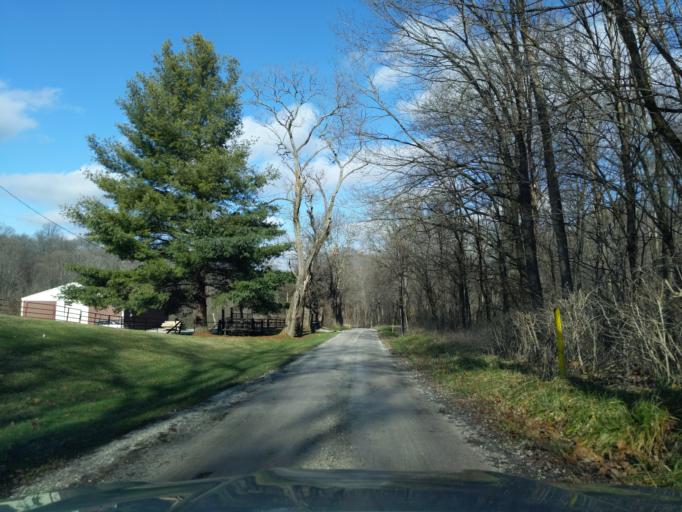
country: US
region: Indiana
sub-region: Decatur County
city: Greensburg
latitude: 39.2492
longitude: -85.4848
